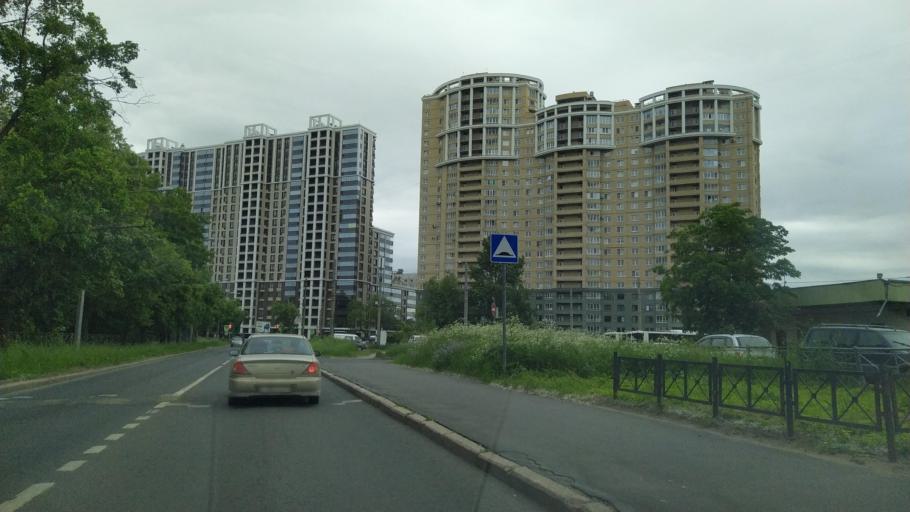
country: RU
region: St.-Petersburg
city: Kupchino
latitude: 59.8426
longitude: 30.3087
